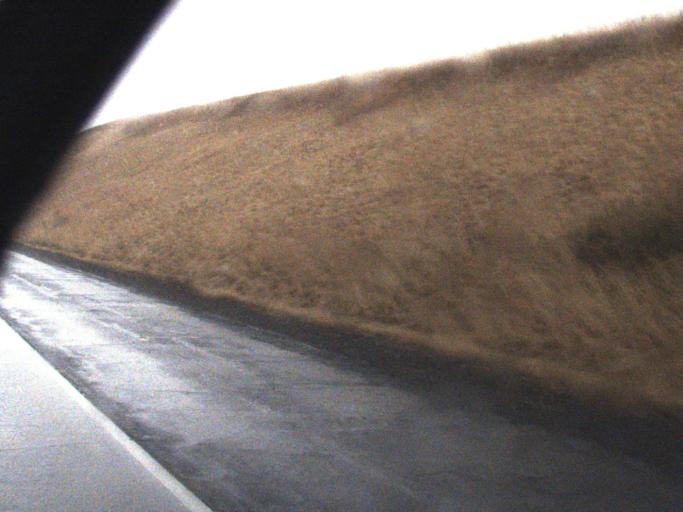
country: US
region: Washington
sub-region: Whitman County
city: Colfax
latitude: 47.0862
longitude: -117.3811
